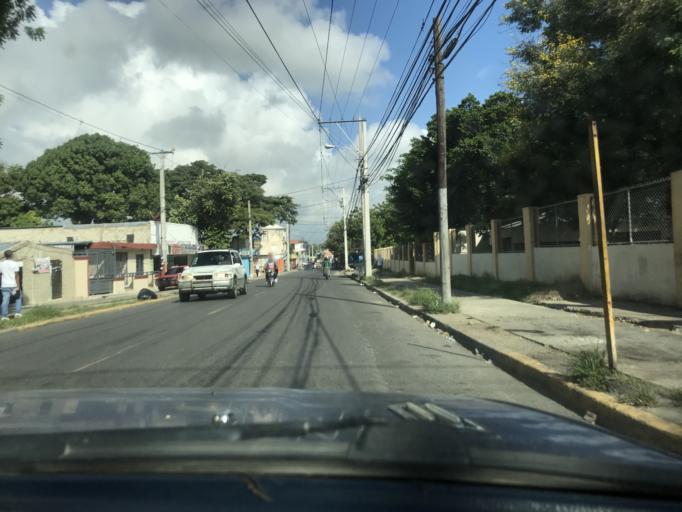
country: DO
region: Santiago
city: Santiago de los Caballeros
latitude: 19.4546
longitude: -70.7179
